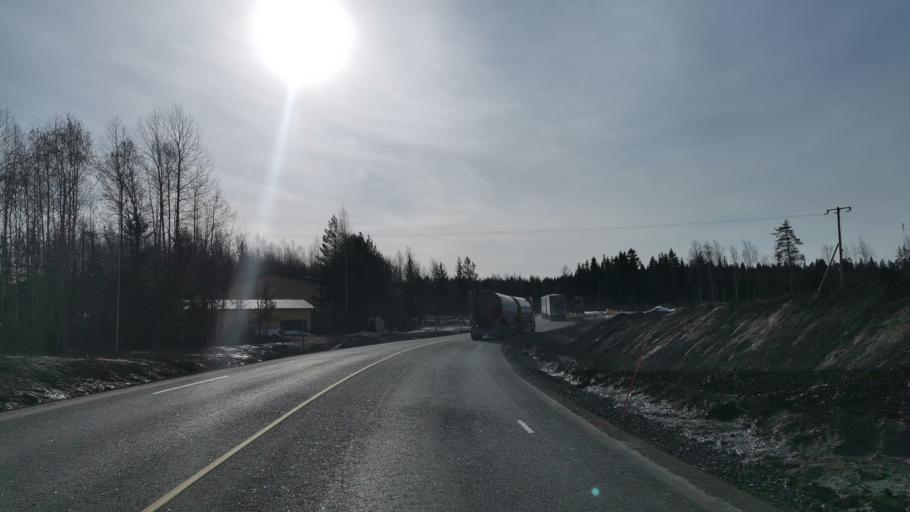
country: FI
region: Kymenlaakso
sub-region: Kouvola
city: Kouvola
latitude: 60.8689
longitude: 26.5507
